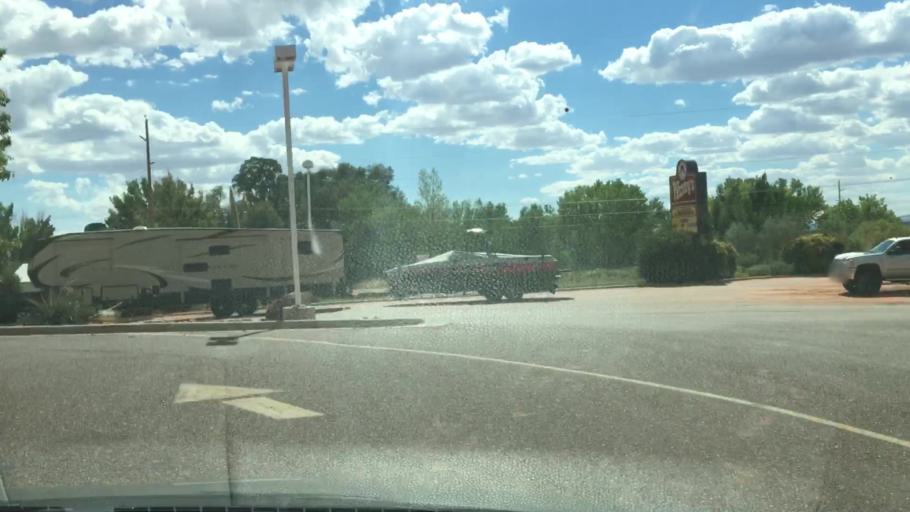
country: US
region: Utah
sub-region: Kane County
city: Kanab
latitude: 37.0432
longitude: -112.5143
